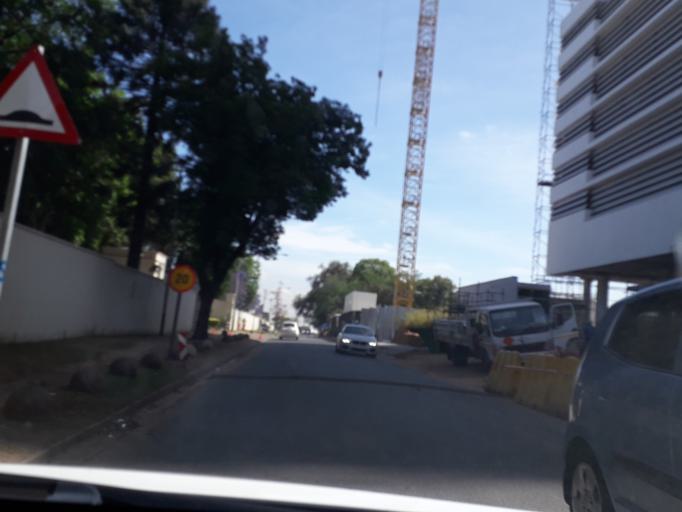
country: ZA
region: Gauteng
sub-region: City of Johannesburg Metropolitan Municipality
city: Johannesburg
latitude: -26.1224
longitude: 28.0466
